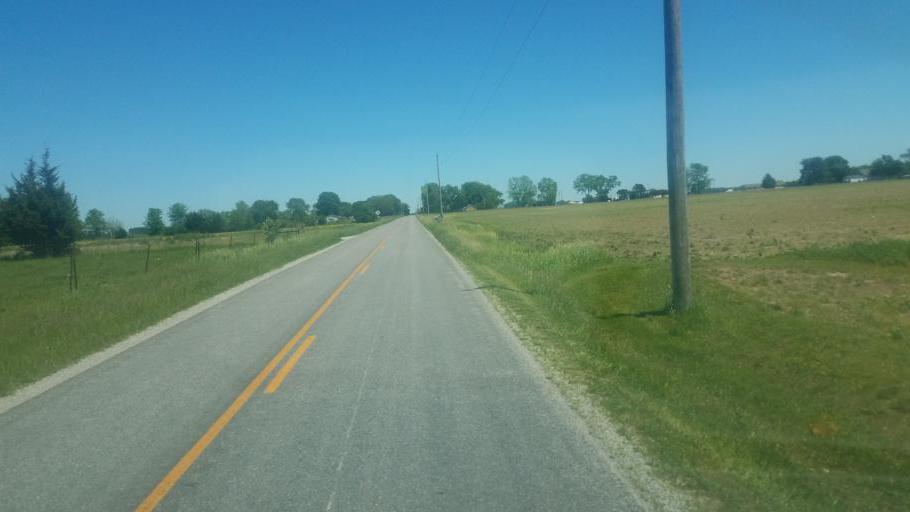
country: US
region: Ohio
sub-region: Shelby County
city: Sidney
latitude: 40.2126
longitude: -84.1391
